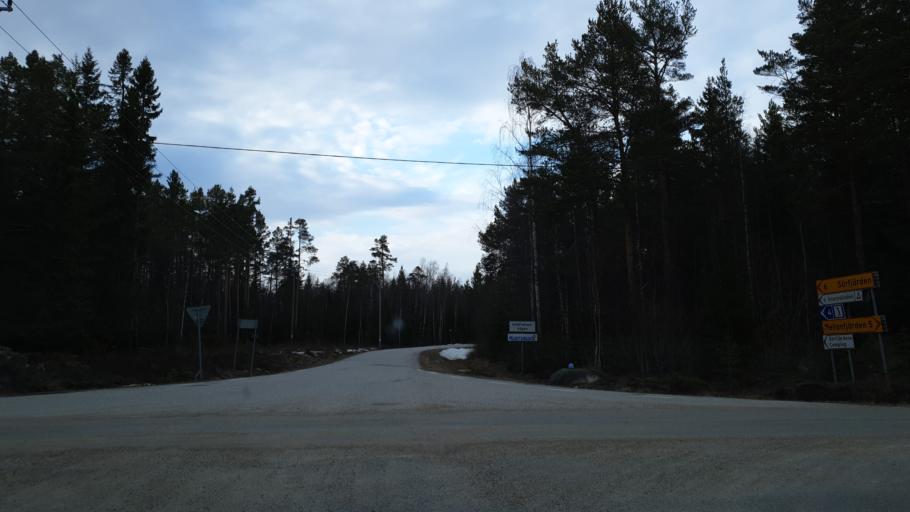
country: SE
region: Vaesternorrland
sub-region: Sundsvalls Kommun
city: Njurundabommen
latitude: 61.9886
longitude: 17.3773
